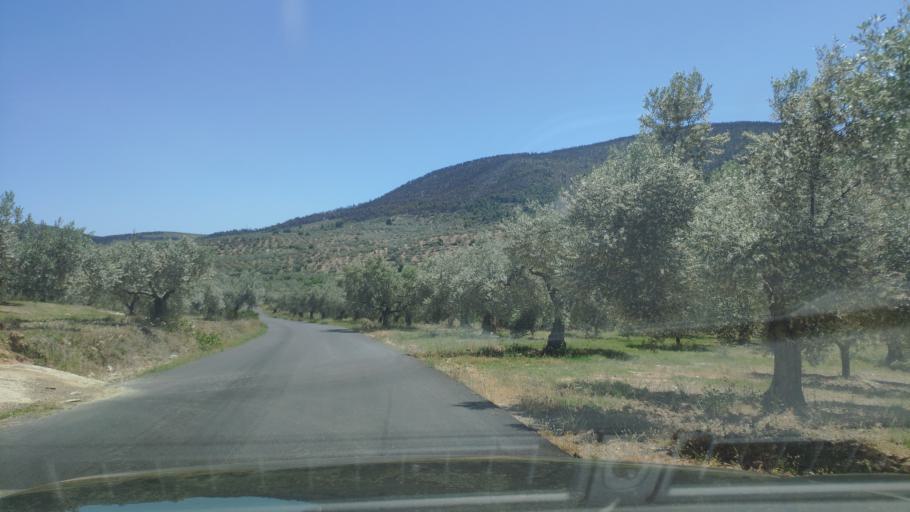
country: GR
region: Peloponnese
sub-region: Nomos Korinthias
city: Athikia
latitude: 37.8066
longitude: 22.9099
